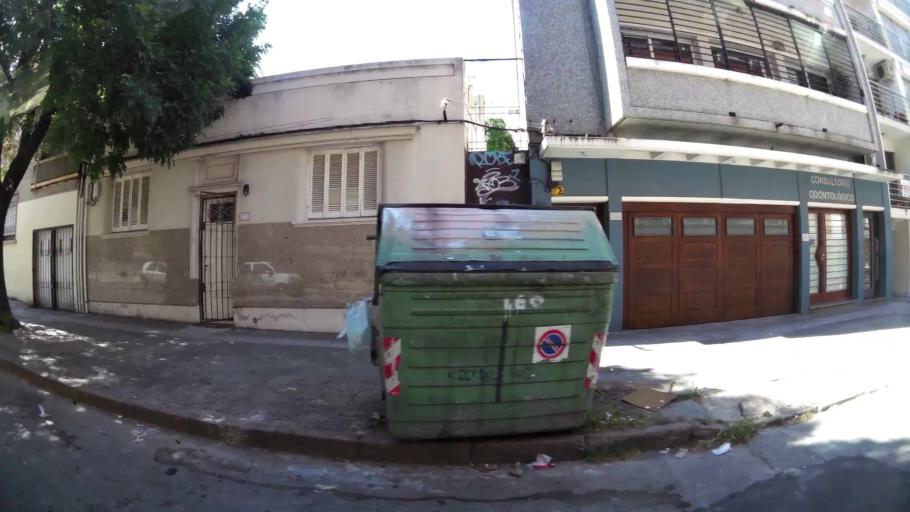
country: UY
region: Montevideo
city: Montevideo
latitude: -34.9041
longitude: -56.1573
